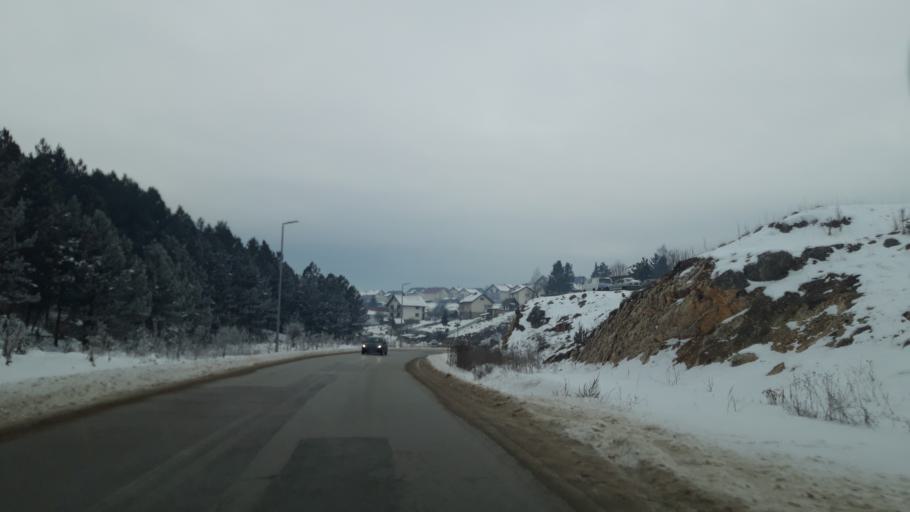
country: BA
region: Republika Srpska
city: Sokolac
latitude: 43.9366
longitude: 18.8099
